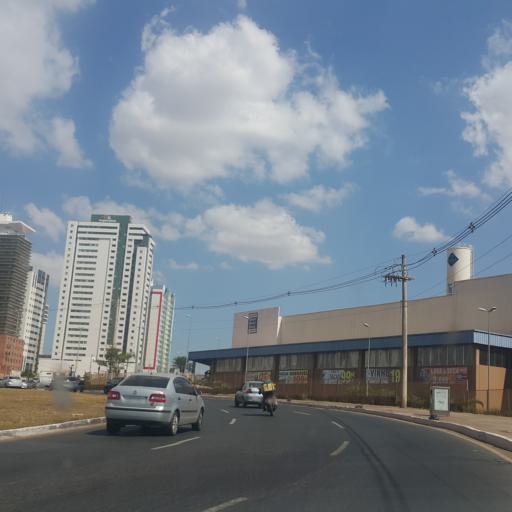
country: BR
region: Federal District
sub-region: Brasilia
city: Brasilia
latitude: -15.8324
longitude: -48.0391
